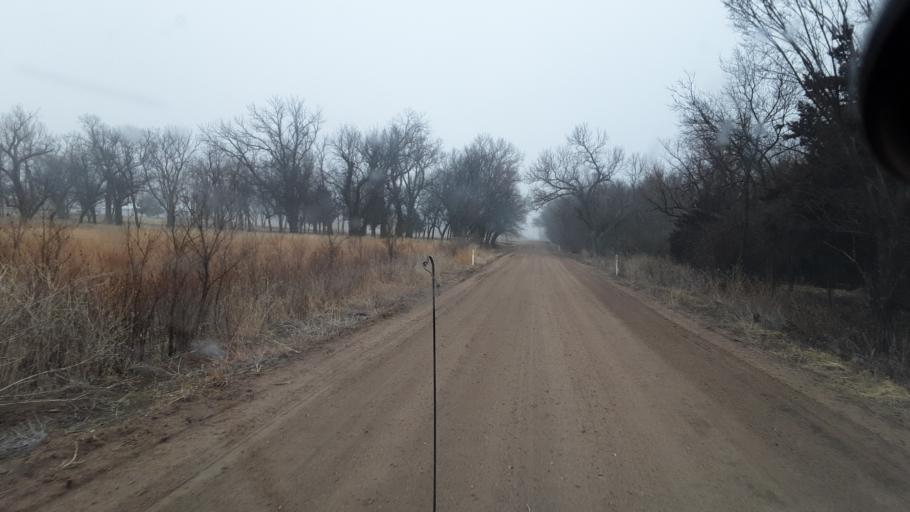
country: US
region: Kansas
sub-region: Reno County
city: South Hutchinson
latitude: 37.9024
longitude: -97.9956
